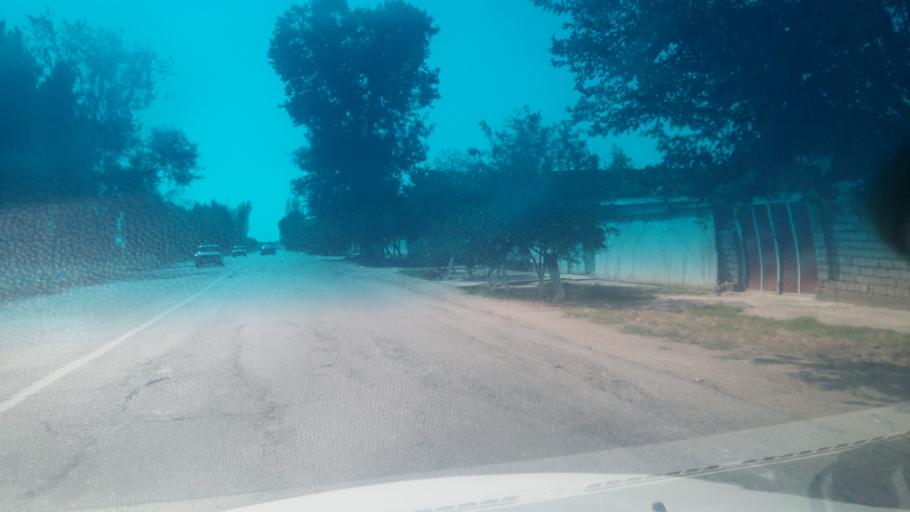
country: UZ
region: Sirdaryo
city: Sirdaryo
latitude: 40.8116
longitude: 68.6754
